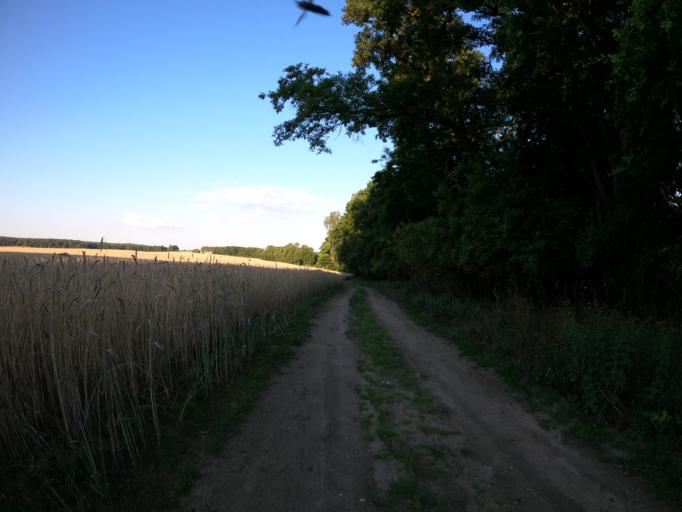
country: DE
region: Brandenburg
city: Althuttendorf
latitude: 53.0261
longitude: 13.8750
